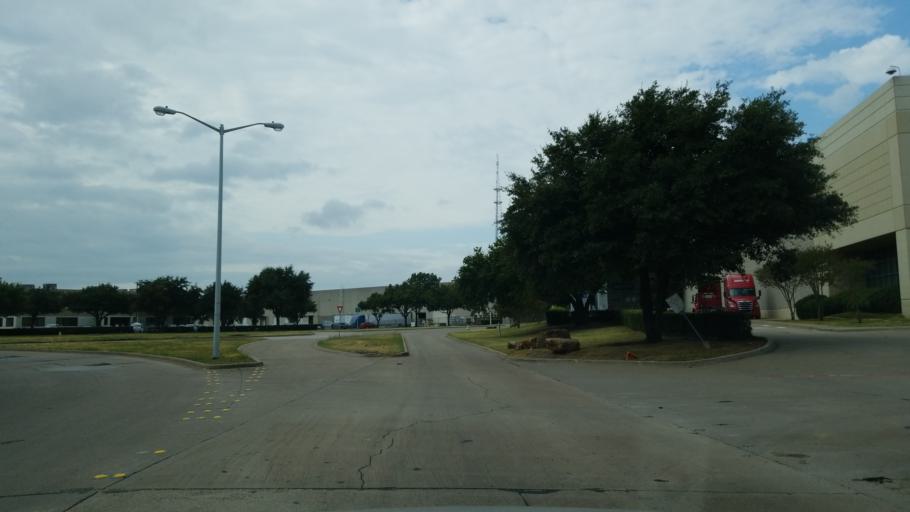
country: US
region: Texas
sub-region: Dallas County
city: Garland
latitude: 32.9054
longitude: -96.6804
